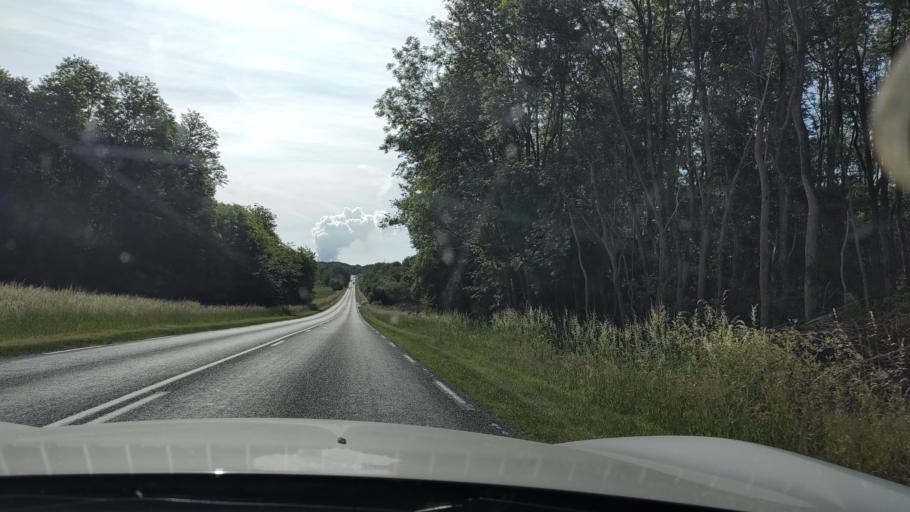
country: FR
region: Ile-de-France
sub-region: Departement de Seine-et-Marne
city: Sourdun
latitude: 48.5322
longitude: 3.3810
